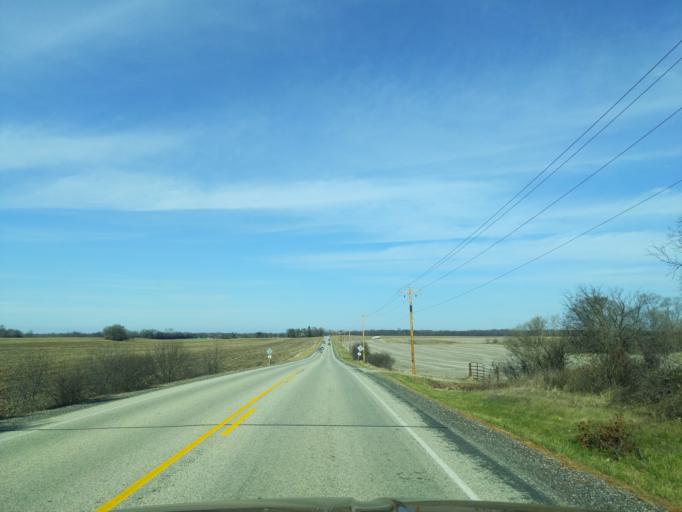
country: US
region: Wisconsin
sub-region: Walworth County
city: Elkhorn
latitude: 42.7369
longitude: -88.5921
